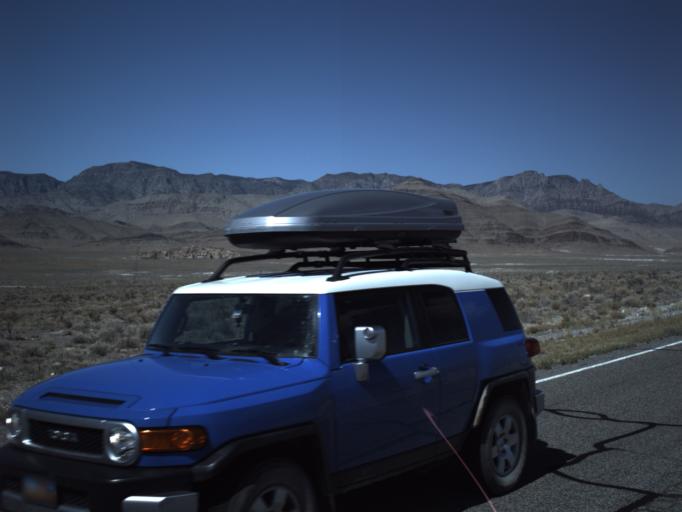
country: US
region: Utah
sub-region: Beaver County
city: Milford
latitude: 39.0275
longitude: -113.3762
